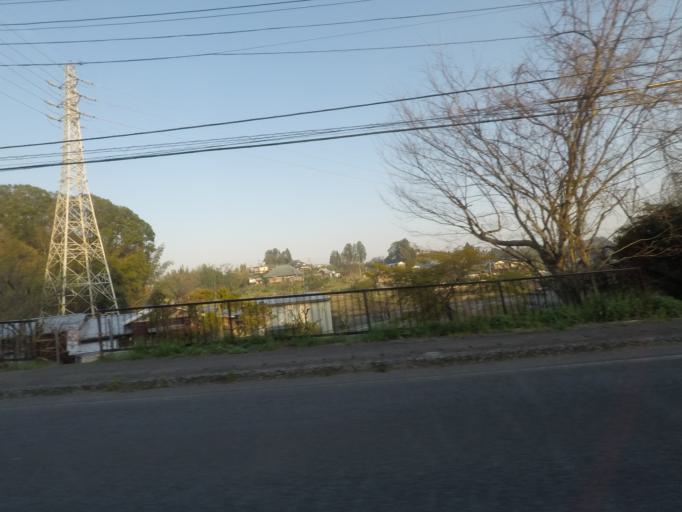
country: JP
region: Chiba
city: Shisui
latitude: 35.7473
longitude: 140.2909
